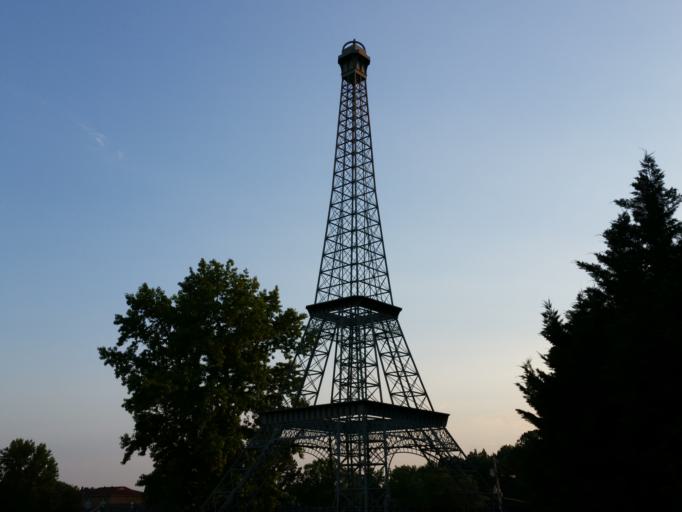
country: US
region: Tennessee
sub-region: Henry County
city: Paris
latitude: 36.2871
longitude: -88.3013
